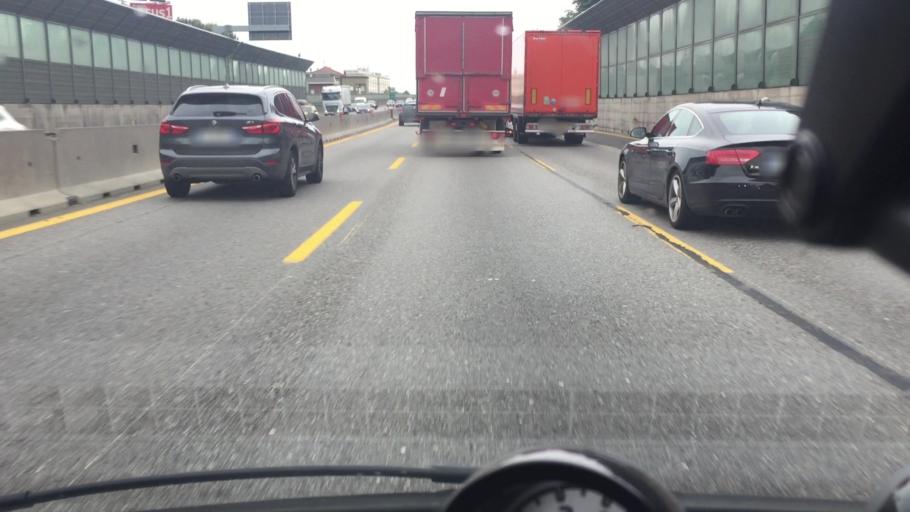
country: IT
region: Lombardy
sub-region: Citta metropolitana di Milano
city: Cinisello Balsamo
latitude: 45.5500
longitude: 9.2272
